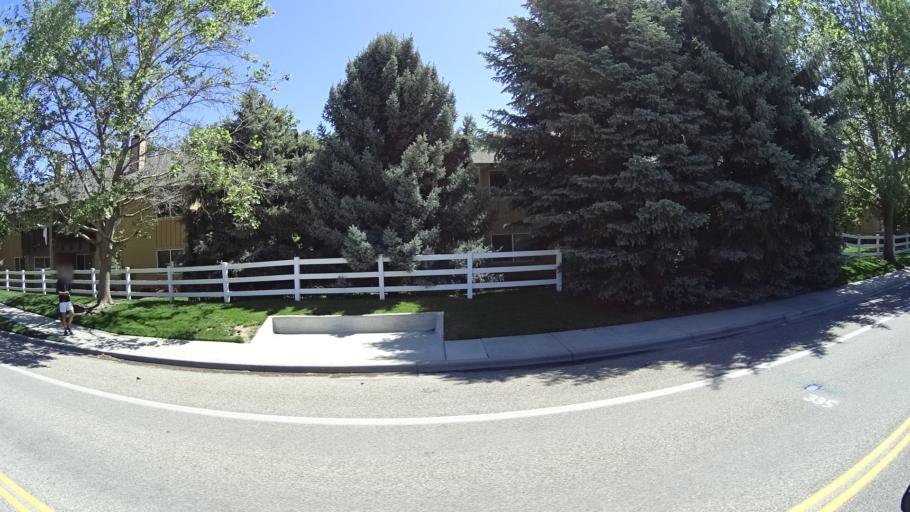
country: US
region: Idaho
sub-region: Ada County
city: Boise
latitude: 43.5729
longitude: -116.1835
